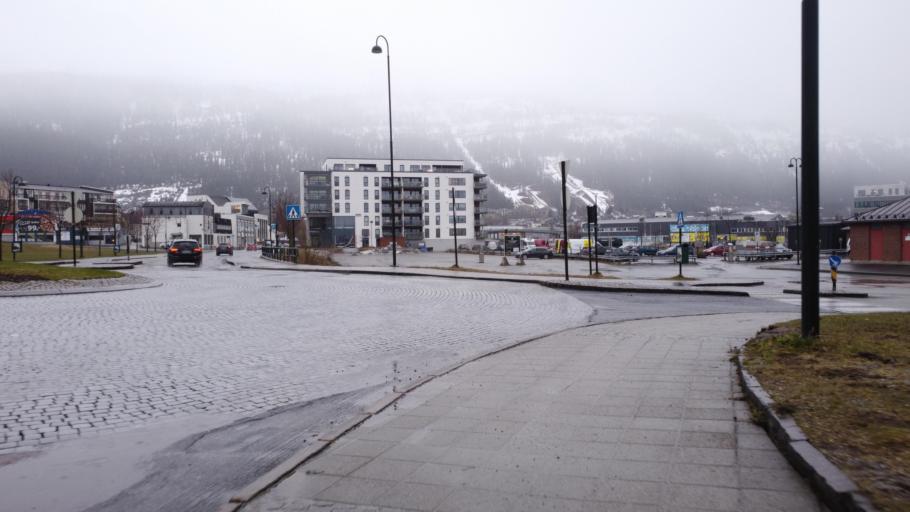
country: NO
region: Nordland
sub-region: Rana
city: Mo i Rana
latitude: 66.3096
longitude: 14.1348
